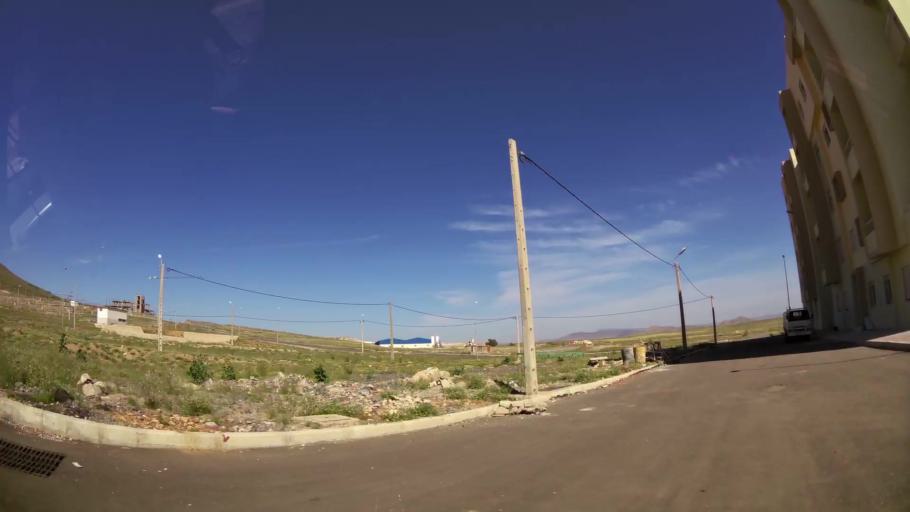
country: MA
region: Oriental
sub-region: Oujda-Angad
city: Oujda
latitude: 34.6499
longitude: -1.9549
